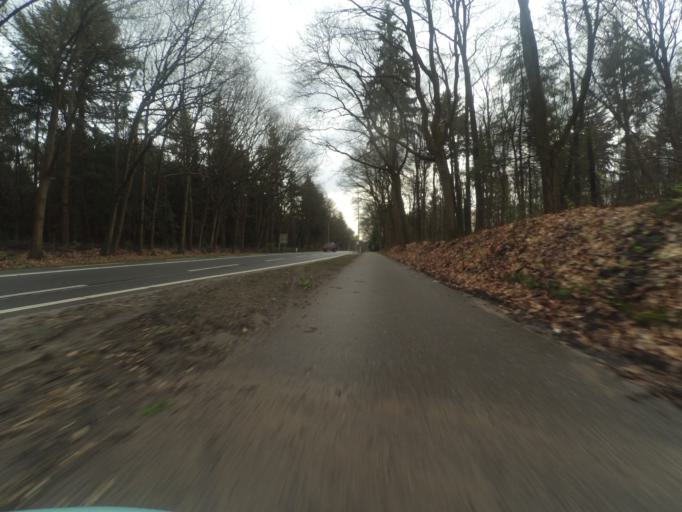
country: NL
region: Gelderland
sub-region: Gemeente Apeldoorn
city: Beekbergen
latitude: 52.1527
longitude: 5.9596
